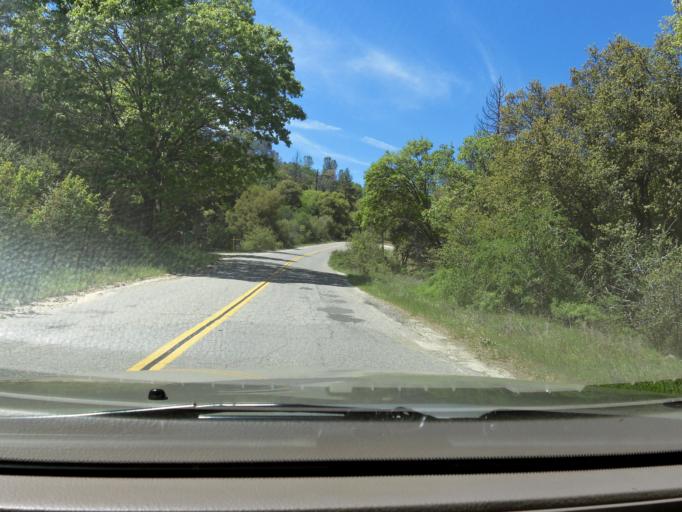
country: US
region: California
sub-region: Fresno County
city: Auberry
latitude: 37.2340
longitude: -119.5142
